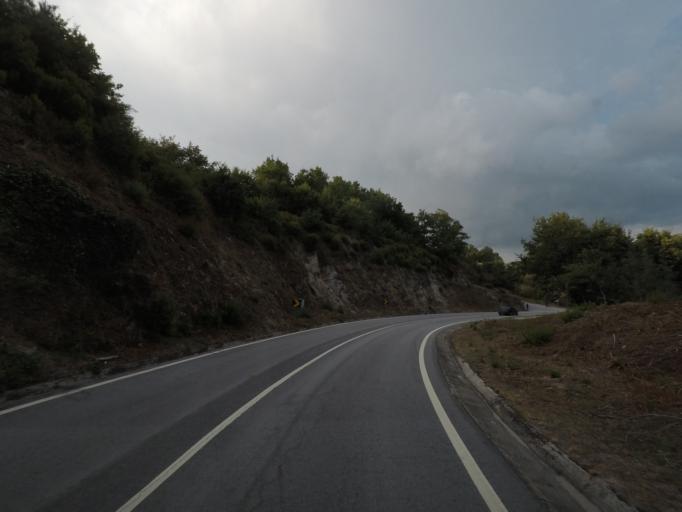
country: PT
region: Porto
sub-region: Baiao
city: Valadares
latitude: 41.2093
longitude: -7.9794
